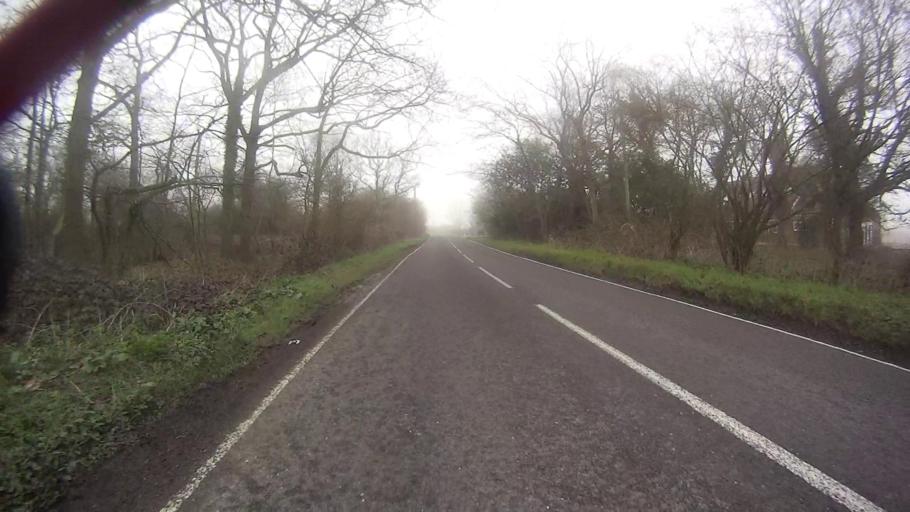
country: GB
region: England
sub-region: Surrey
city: Newdigate
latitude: 51.1372
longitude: -0.3163
